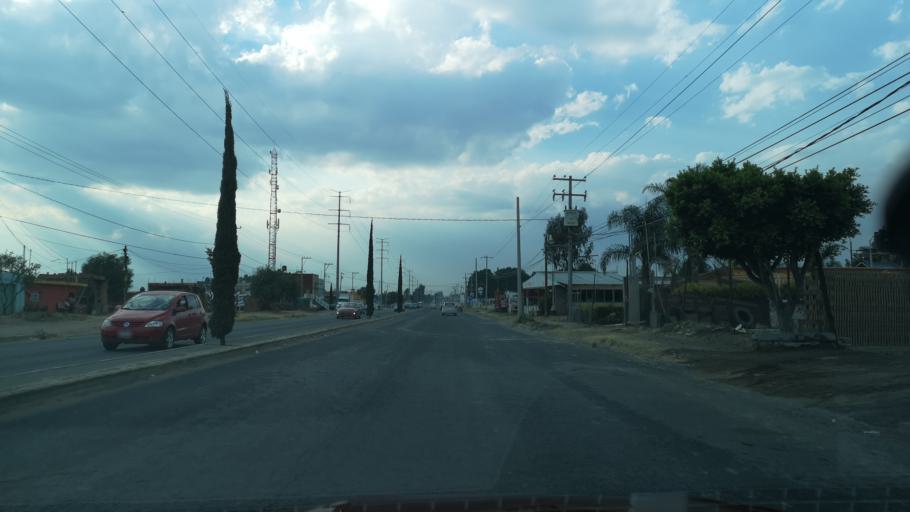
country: MX
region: Puebla
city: Cuanala
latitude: 19.0873
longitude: -98.3332
